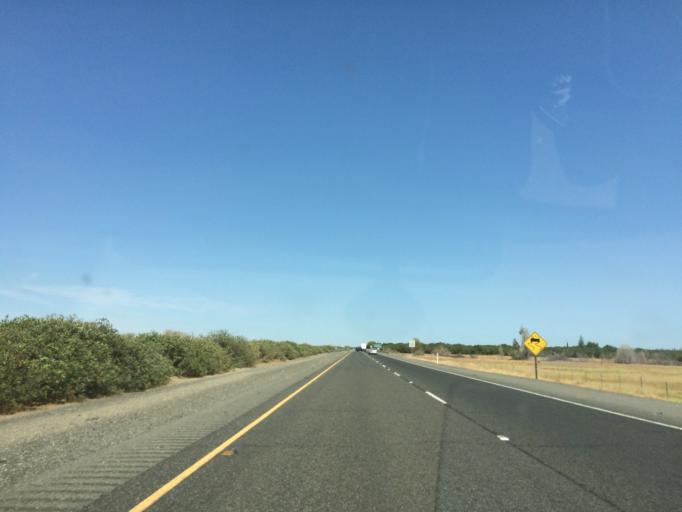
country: US
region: California
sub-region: Glenn County
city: Willows
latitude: 39.6315
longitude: -122.2041
